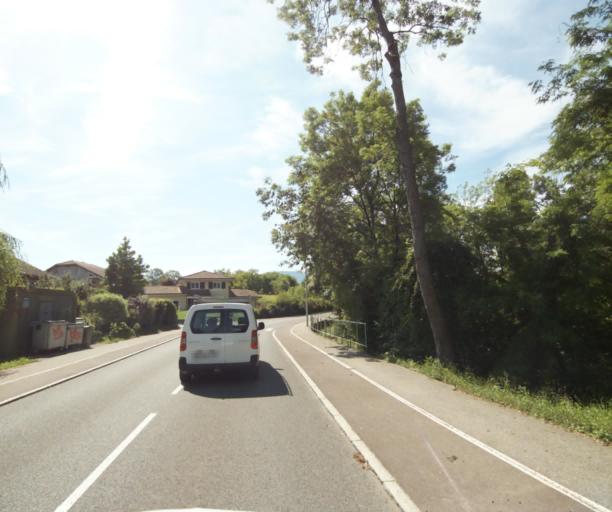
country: FR
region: Rhone-Alpes
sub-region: Departement de la Haute-Savoie
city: Margencel
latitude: 46.3394
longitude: 6.4165
